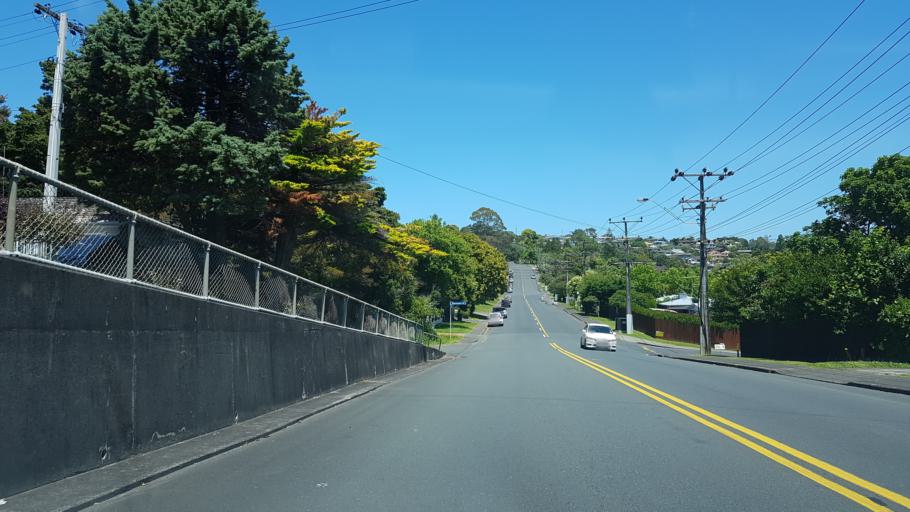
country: NZ
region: Auckland
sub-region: Auckland
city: North Shore
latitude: -36.7879
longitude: 174.7302
